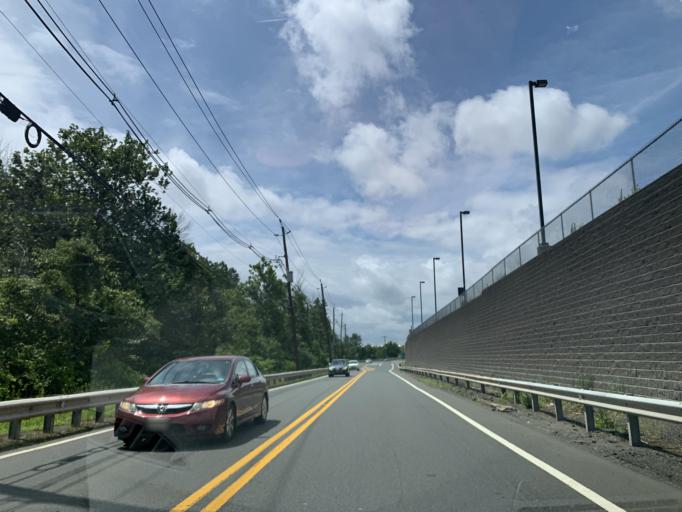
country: US
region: New Jersey
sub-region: Somerset County
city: Martinsville
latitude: 40.5815
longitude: -74.5575
